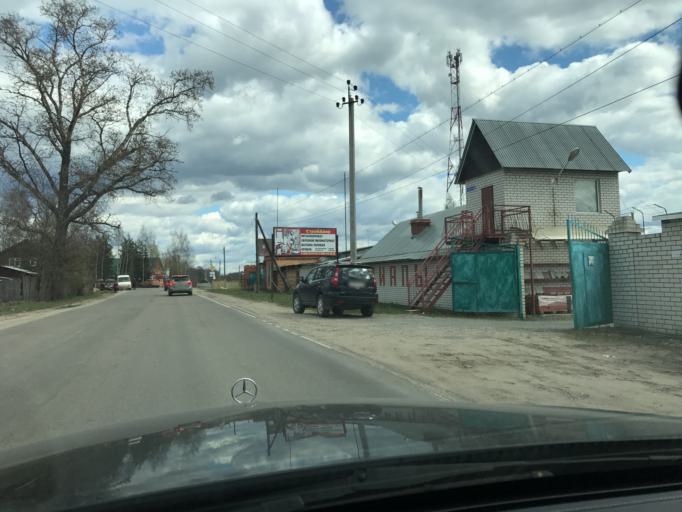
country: RU
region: Vladimir
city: Pokrov
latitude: 55.8912
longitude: 39.2122
